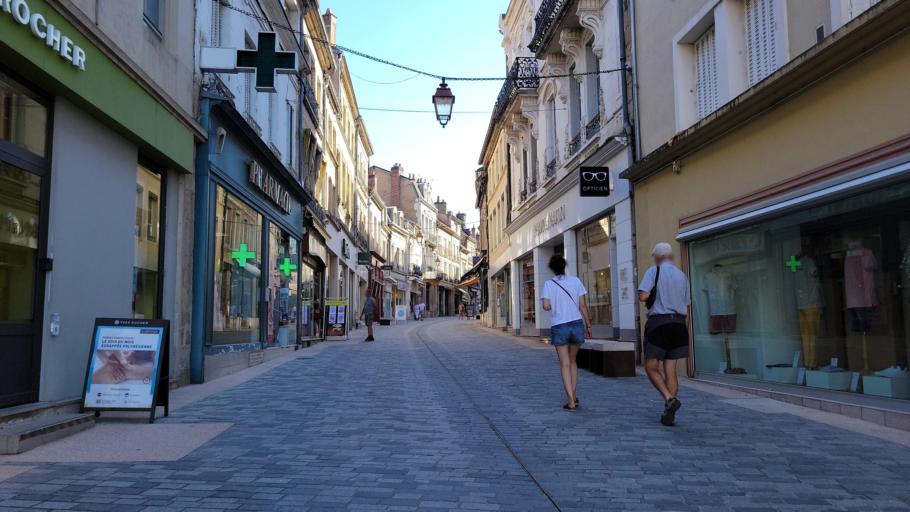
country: FR
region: Bourgogne
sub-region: Departement de Saone-et-Loire
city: Autun
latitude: 46.9496
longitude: 4.2995
